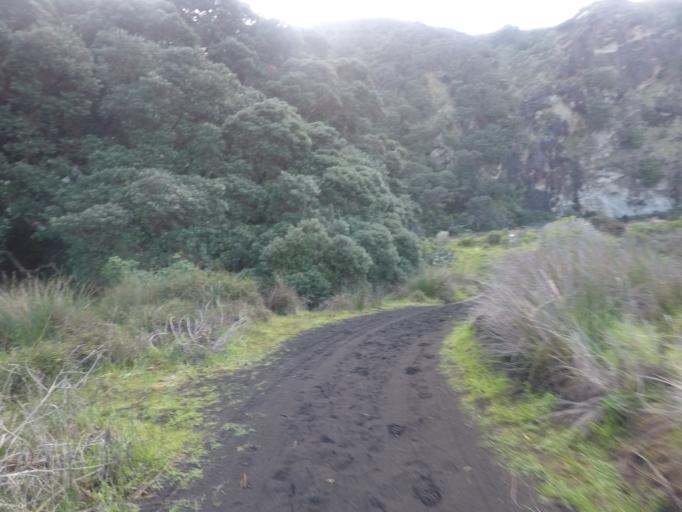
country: NZ
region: Auckland
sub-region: Auckland
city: Titirangi
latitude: -37.0038
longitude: 174.4803
